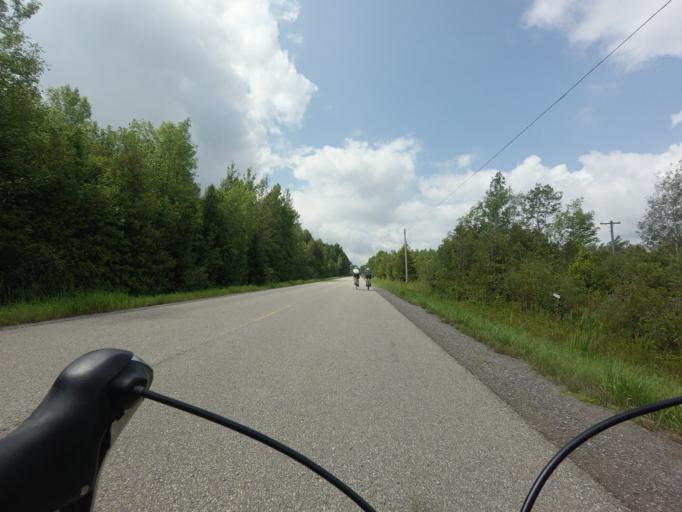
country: CA
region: Ontario
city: Brockville
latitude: 44.8043
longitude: -75.7191
